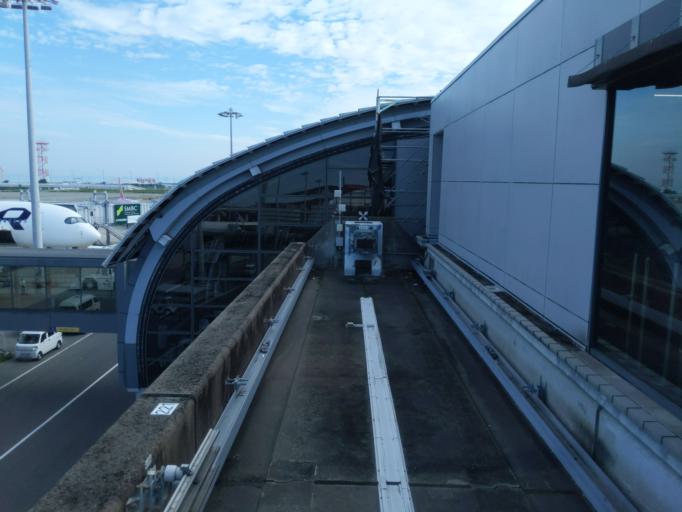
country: JP
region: Osaka
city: Kaizuka
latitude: 34.4388
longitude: 135.2515
